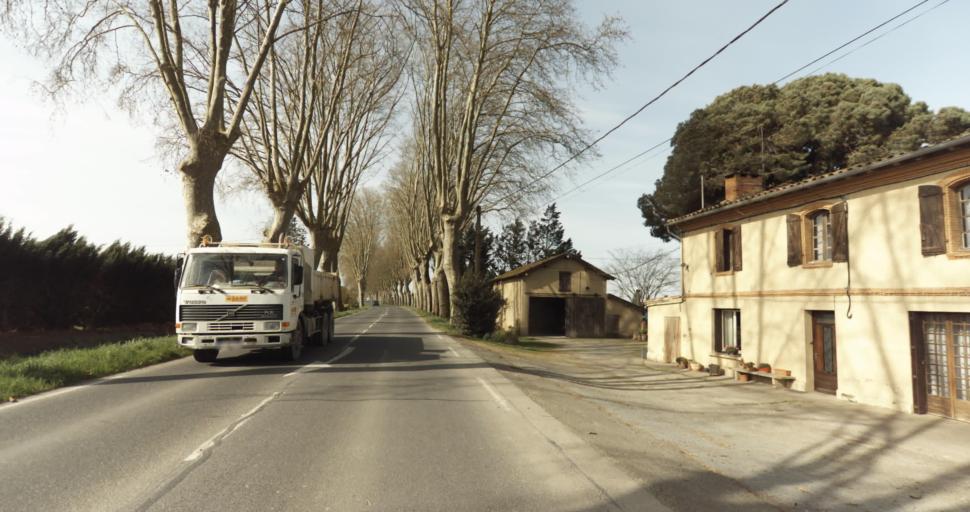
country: FR
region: Midi-Pyrenees
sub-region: Departement du Tarn
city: Saint-Sulpice-la-Pointe
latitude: 43.7814
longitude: 1.6751
